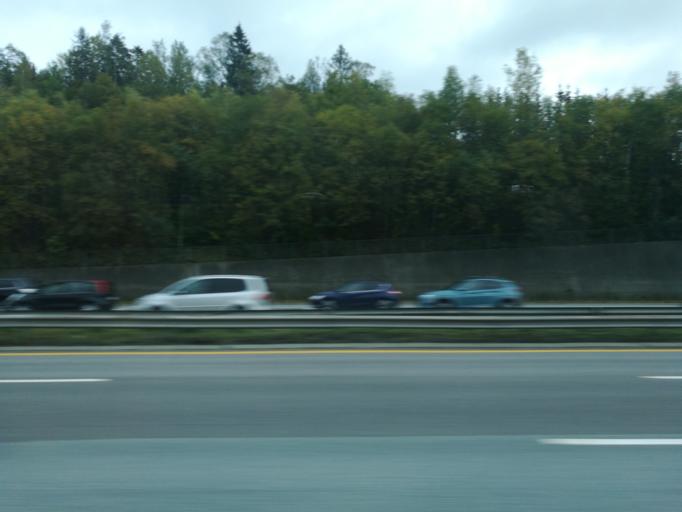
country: NO
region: Akershus
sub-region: Lorenskog
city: Kjenn
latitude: 59.9390
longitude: 10.8960
